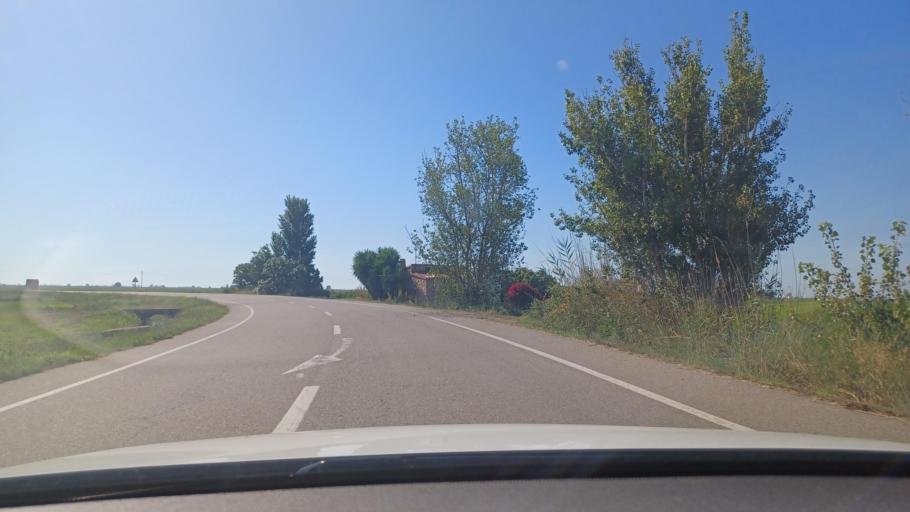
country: ES
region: Catalonia
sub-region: Provincia de Tarragona
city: Amposta
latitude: 40.7054
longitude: 0.6421
